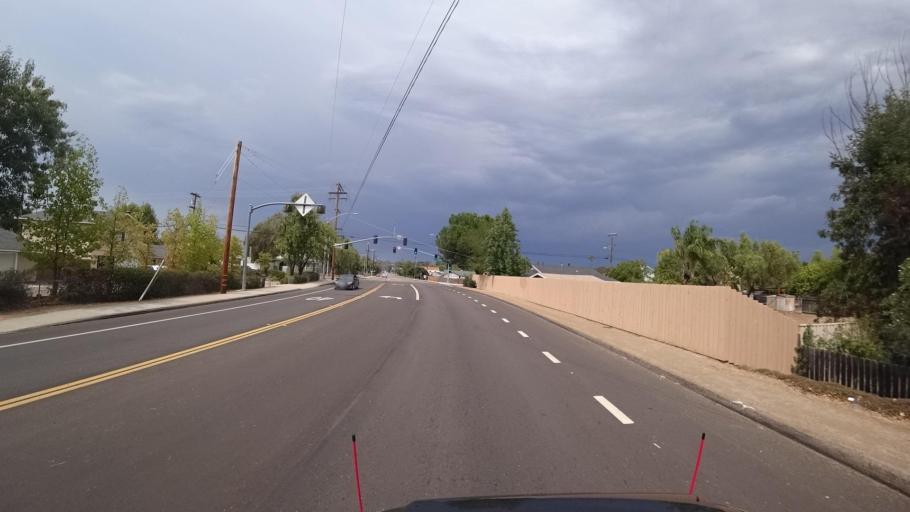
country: US
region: California
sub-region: San Diego County
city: Ramona
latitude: 33.0371
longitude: -116.8648
